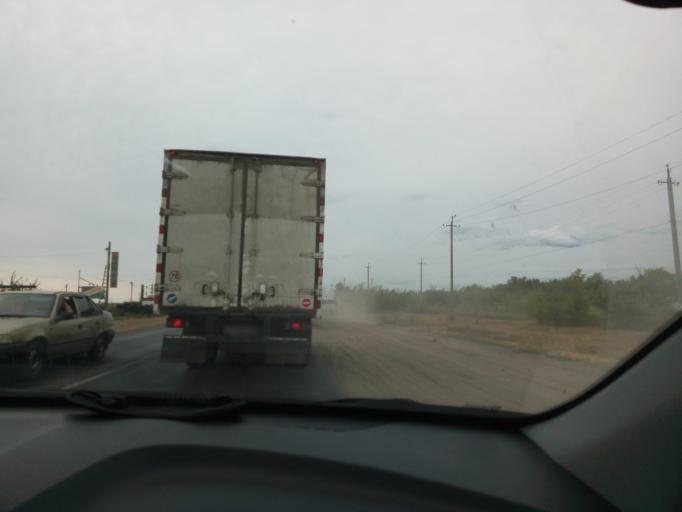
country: RU
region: Volgograd
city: Vodstroy
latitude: 48.8484
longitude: 44.5586
